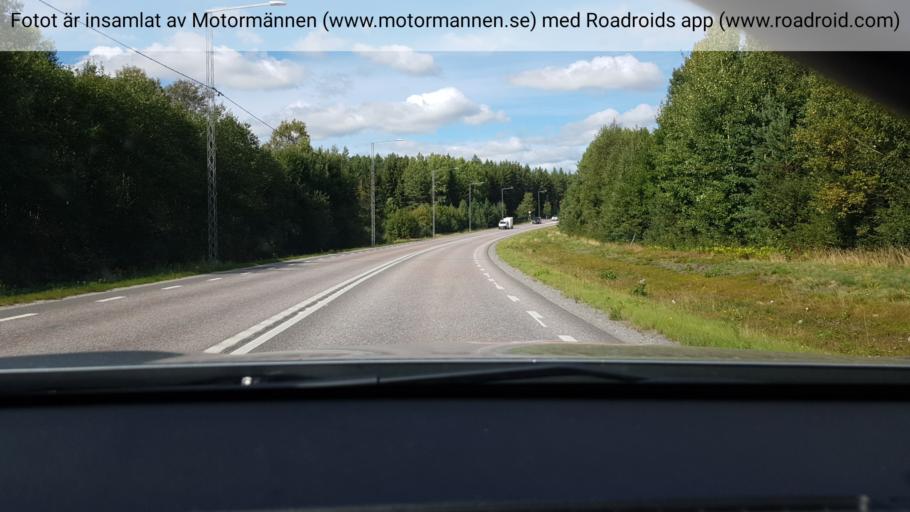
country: SE
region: Stockholm
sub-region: Vallentuna Kommun
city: Vallentuna
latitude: 59.4962
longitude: 18.1029
